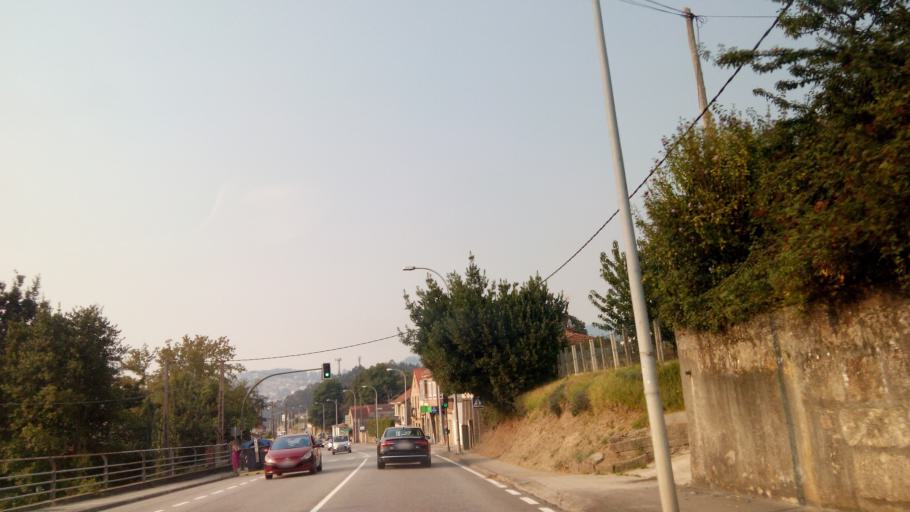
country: ES
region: Galicia
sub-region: Provincia de Pontevedra
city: Nigran
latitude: 42.1250
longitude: -8.8101
